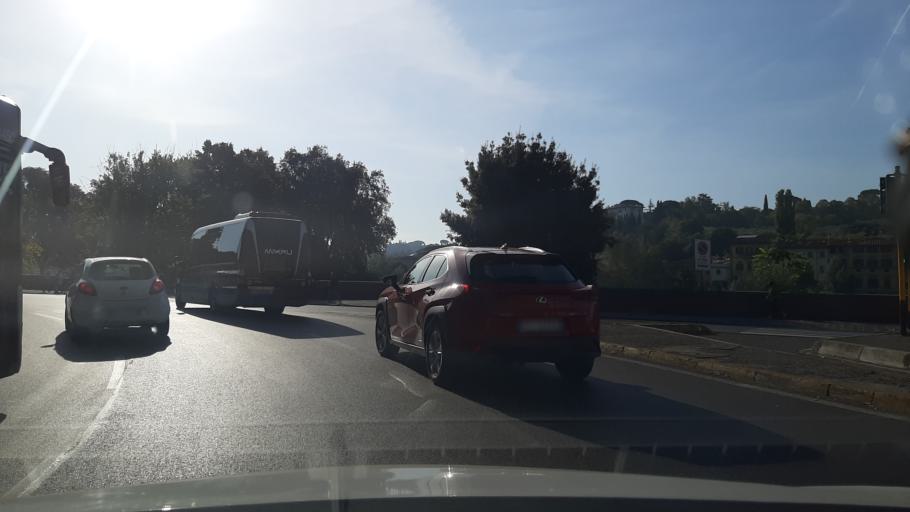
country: IT
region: Tuscany
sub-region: Province of Florence
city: Florence
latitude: 43.7663
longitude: 11.2686
